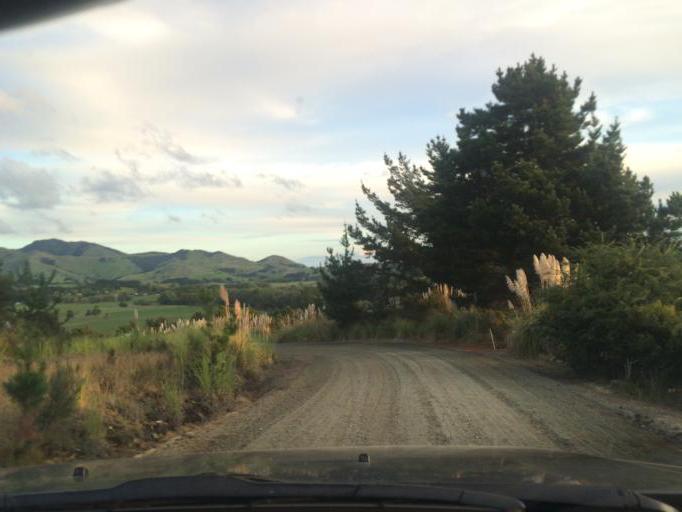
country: NZ
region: Northland
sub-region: Whangarei
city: Maungatapere
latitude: -35.8067
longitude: 174.0416
